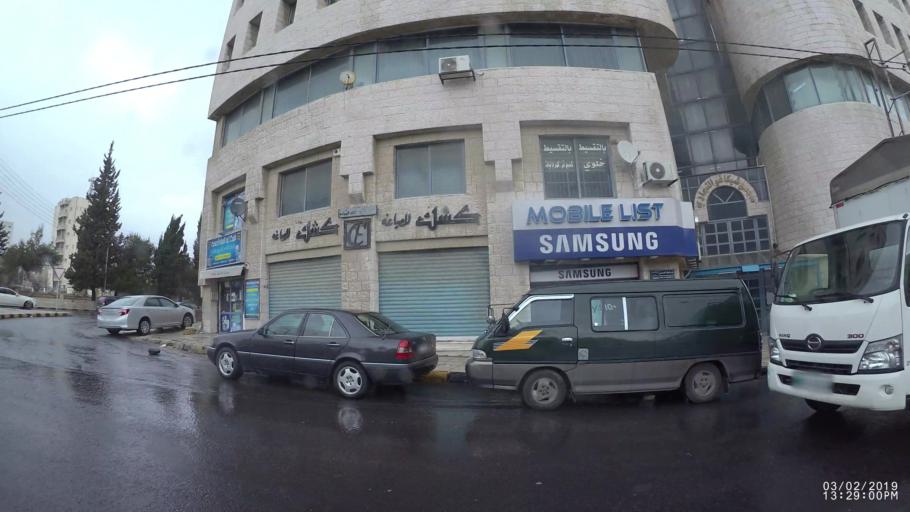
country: JO
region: Amman
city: Amman
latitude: 31.9686
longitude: 35.9088
